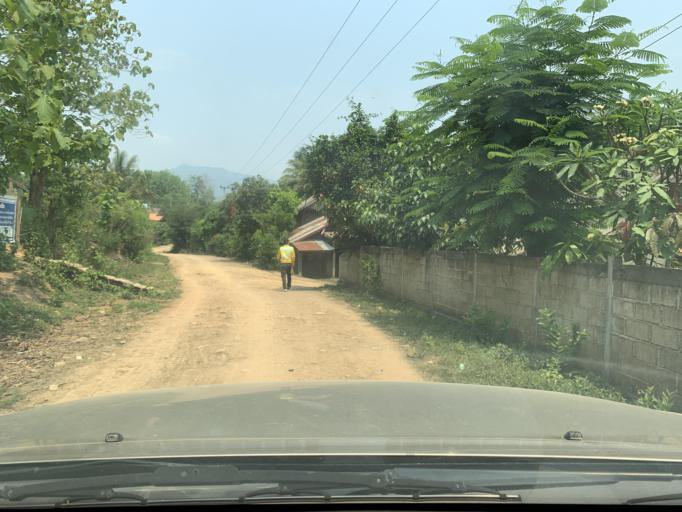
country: LA
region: Louangphabang
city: Louangphabang
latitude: 19.9459
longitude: 102.1342
